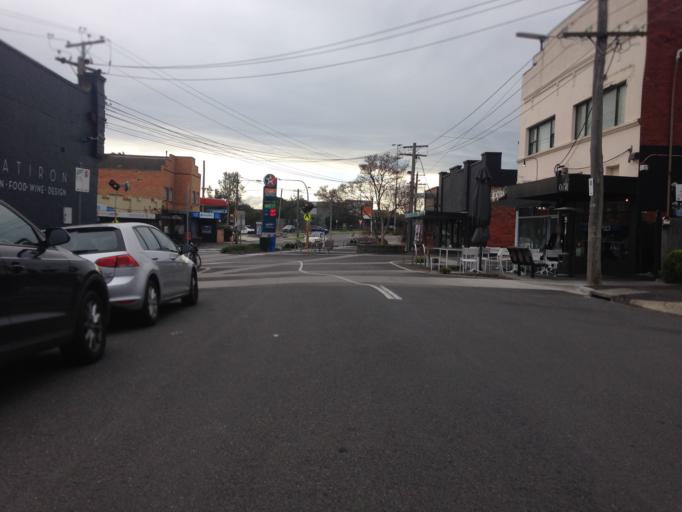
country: AU
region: Victoria
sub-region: Boroondara
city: Kew
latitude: -37.7962
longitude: 145.0360
